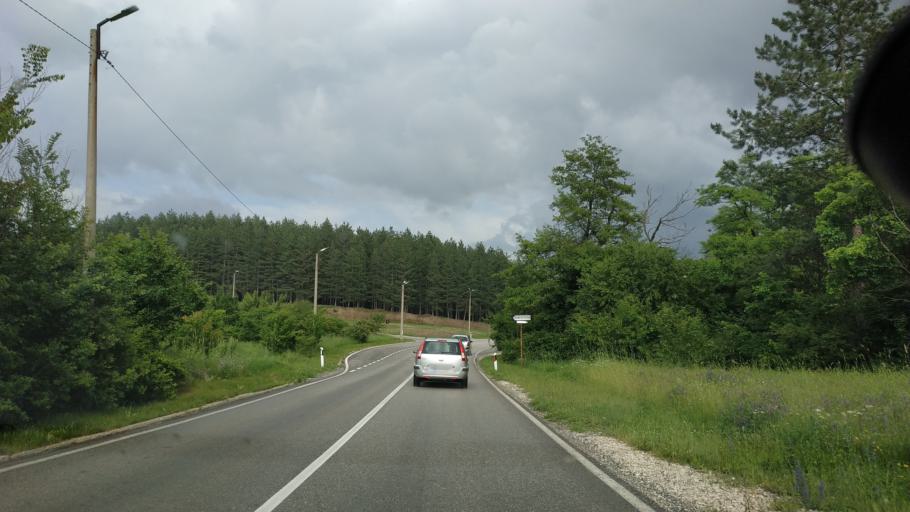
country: RS
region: Central Serbia
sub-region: Borski Okrug
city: Bor
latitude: 44.0605
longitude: 22.0499
